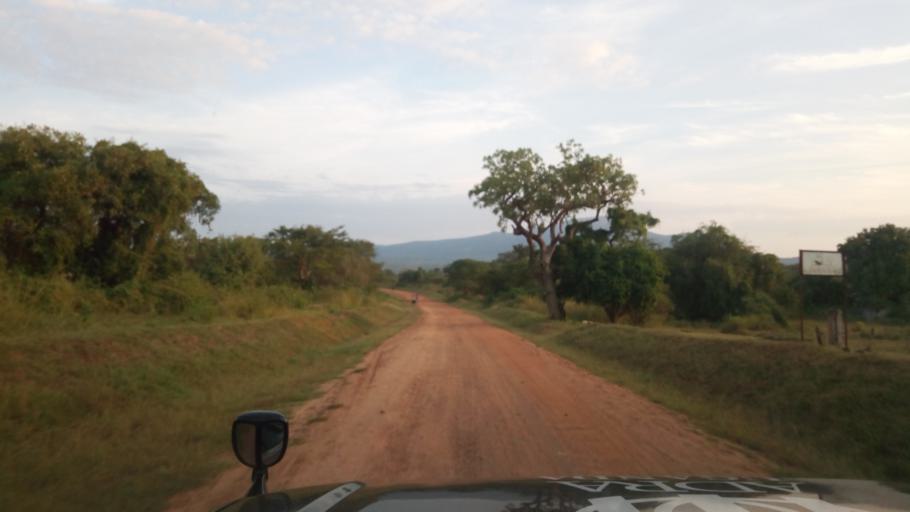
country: UG
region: Northern Region
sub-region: Moyo District
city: Moyo
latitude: 3.5349
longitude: 31.8122
